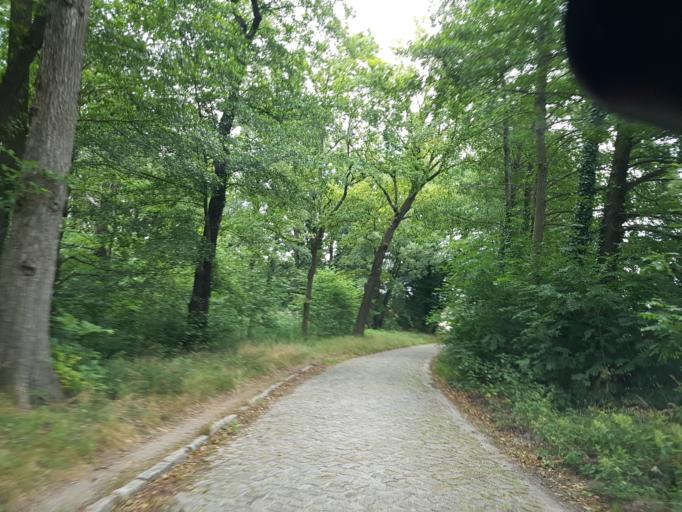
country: DE
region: Brandenburg
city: Sallgast
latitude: 51.5850
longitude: 13.8454
